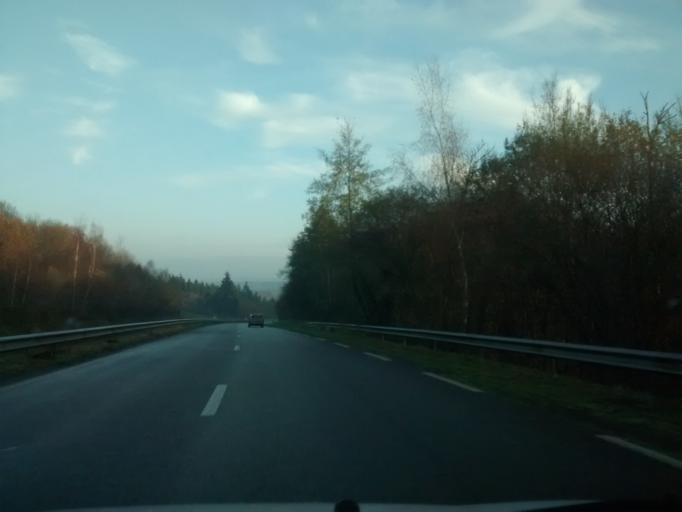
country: FR
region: Brittany
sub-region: Departement d'Ille-et-Vilaine
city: Sens-de-Bretagne
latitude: 48.3590
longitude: -1.5085
